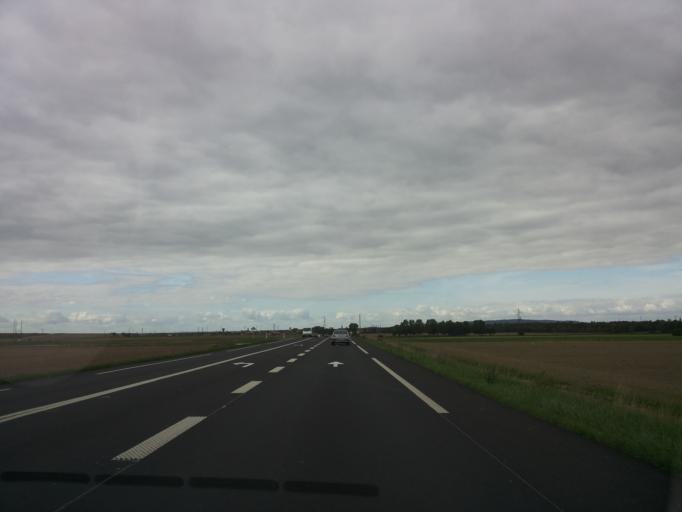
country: FR
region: Champagne-Ardenne
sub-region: Departement de la Marne
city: Verzy
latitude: 49.1581
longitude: 4.2038
